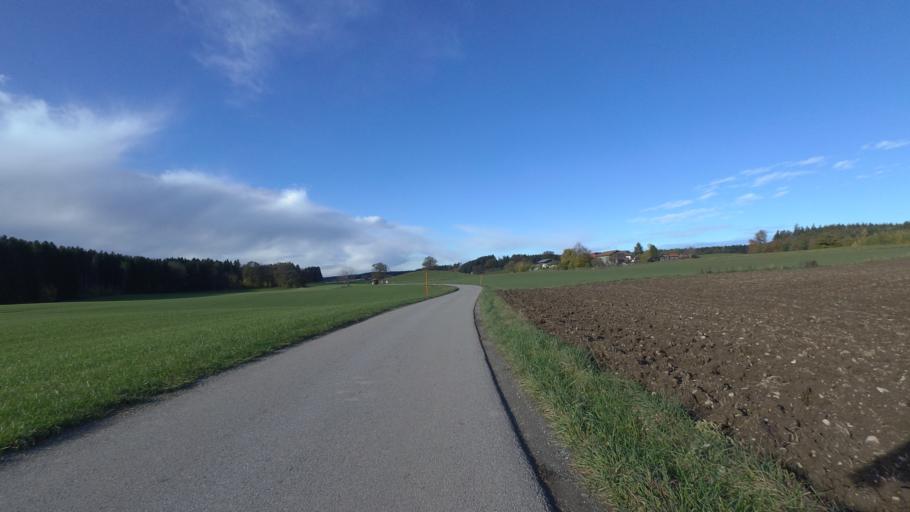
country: DE
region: Bavaria
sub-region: Upper Bavaria
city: Nussdorf
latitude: 47.9230
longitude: 12.5723
